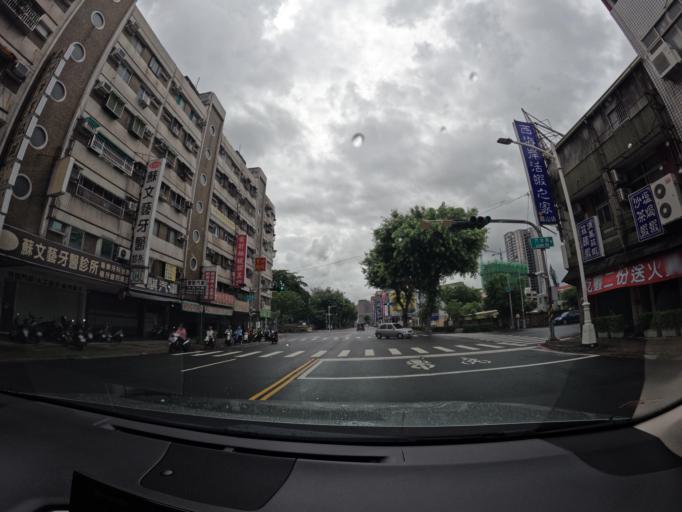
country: TW
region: Kaohsiung
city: Kaohsiung
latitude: 22.6339
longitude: 120.3194
